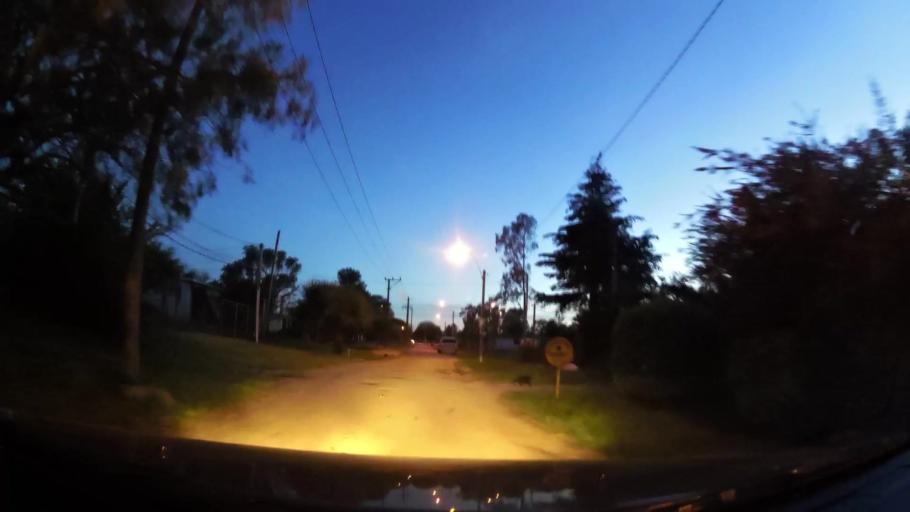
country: UY
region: Canelones
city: Atlantida
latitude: -34.7650
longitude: -55.7617
